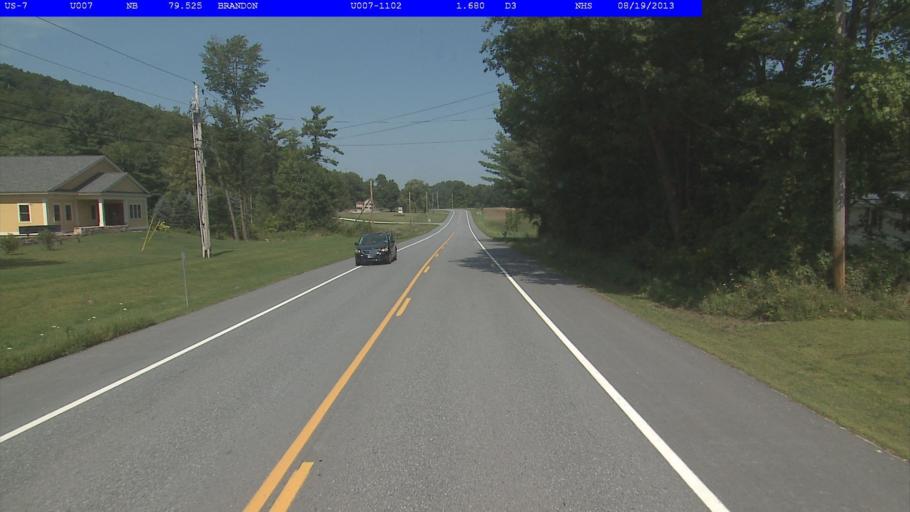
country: US
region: Vermont
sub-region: Rutland County
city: Brandon
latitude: 43.7776
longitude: -73.0561
